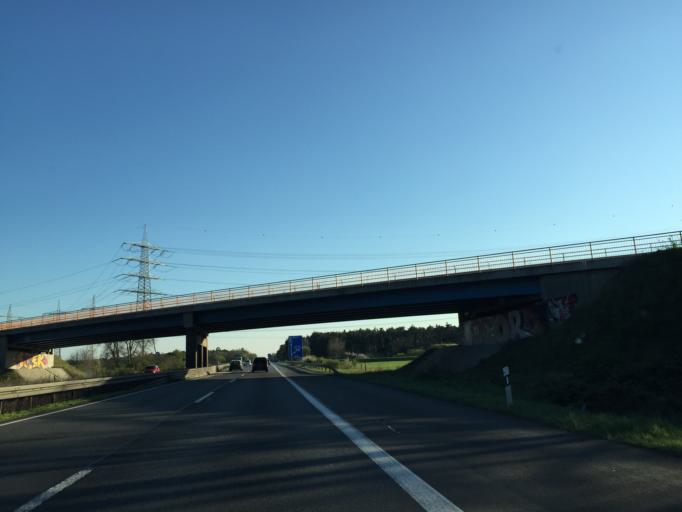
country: DE
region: Hesse
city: Pfungstadt
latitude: 49.8220
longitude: 8.5845
